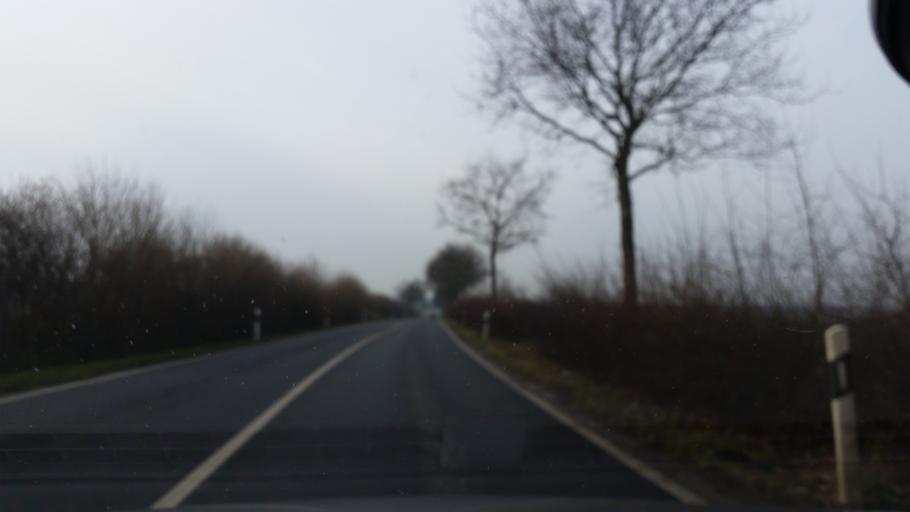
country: DE
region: Lower Saxony
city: Seelze
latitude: 52.3711
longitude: 9.5870
